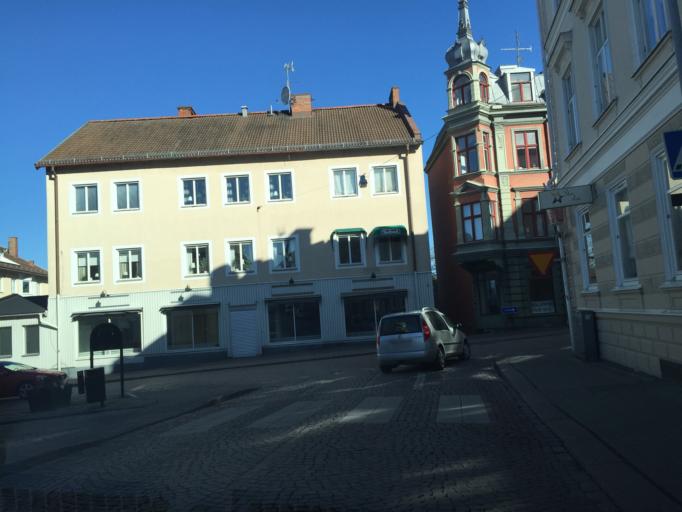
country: SE
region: Kalmar
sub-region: Oskarshamns Kommun
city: Oskarshamn
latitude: 57.2650
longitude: 16.4451
